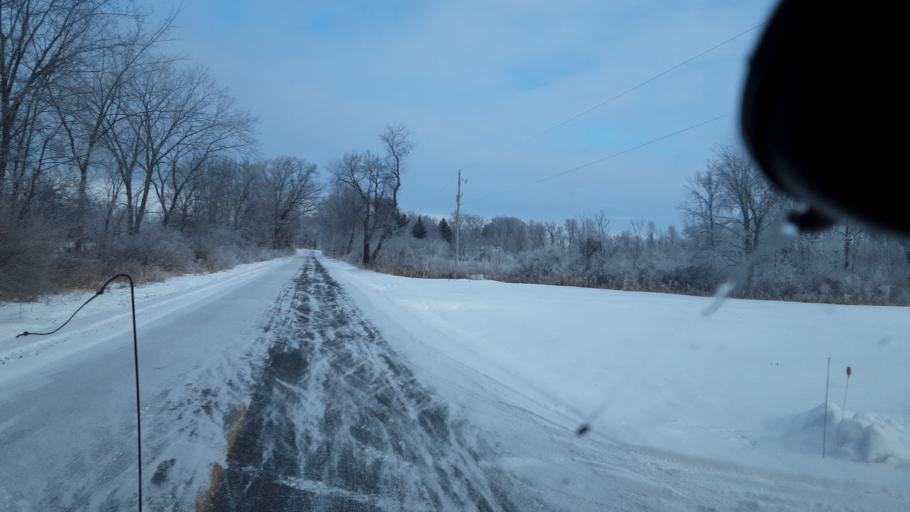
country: US
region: Michigan
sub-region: Ingham County
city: Leslie
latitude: 42.4181
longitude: -84.4823
